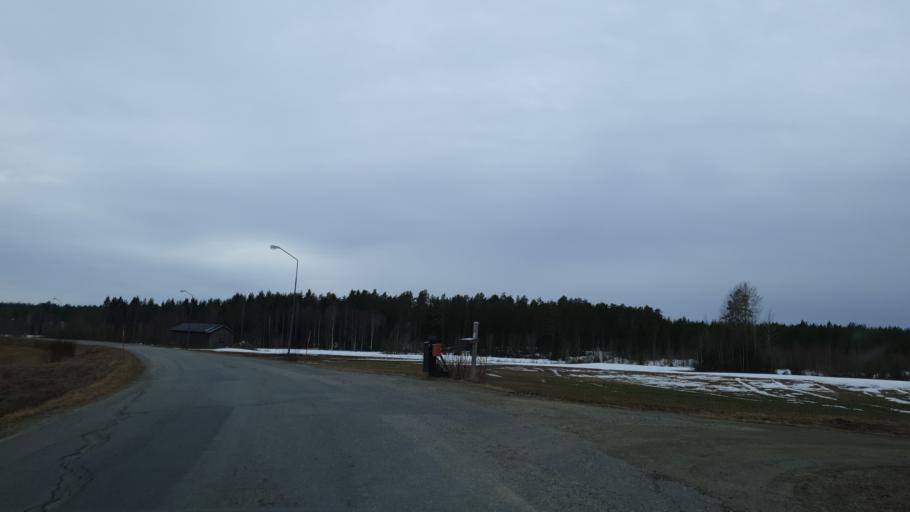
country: SE
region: Vaesterbotten
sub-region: Robertsfors Kommun
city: Robertsfors
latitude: 64.3999
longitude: 21.0036
